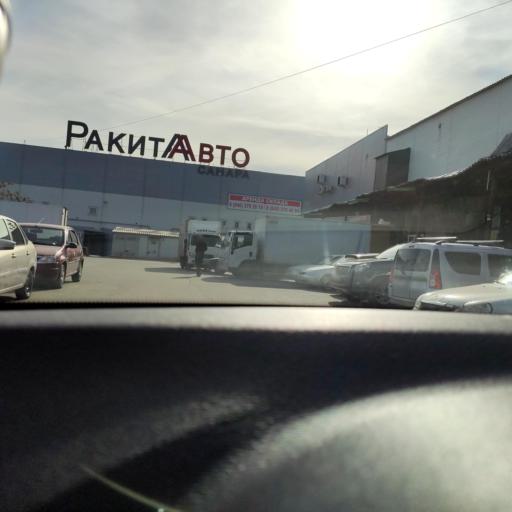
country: RU
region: Samara
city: Petra-Dubrava
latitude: 53.2762
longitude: 50.2737
